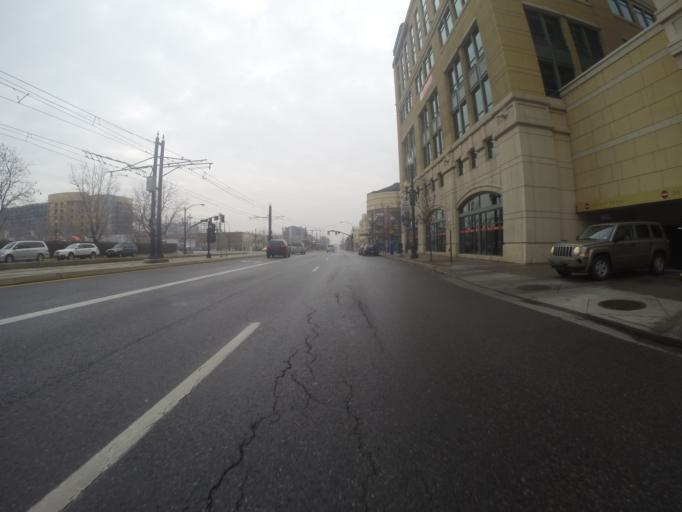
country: US
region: Utah
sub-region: Salt Lake County
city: Salt Lake City
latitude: 40.7680
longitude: -111.9028
